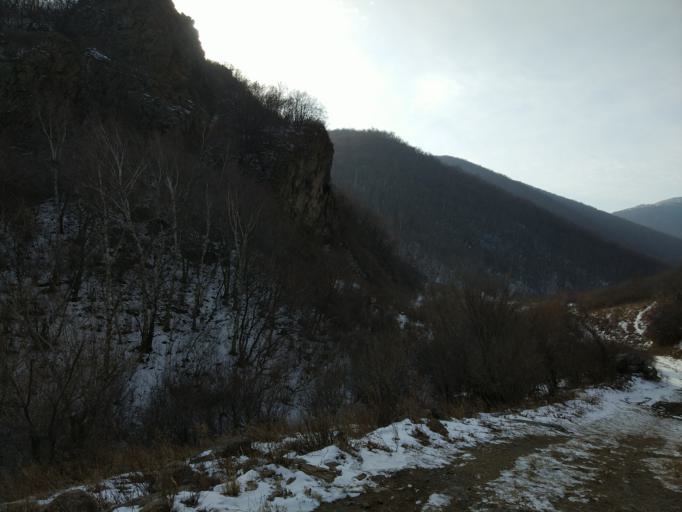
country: CN
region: Hebei
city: Xiwanzi
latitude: 40.8421
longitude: 115.4598
